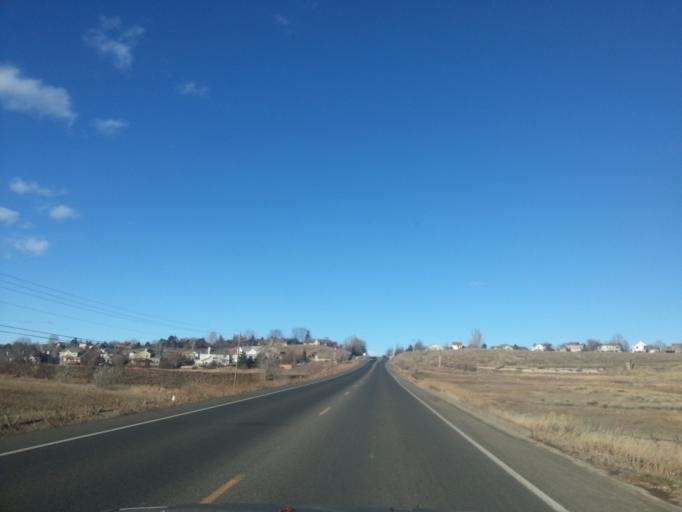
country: US
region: Colorado
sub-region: Larimer County
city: Fort Collins
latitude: 40.5211
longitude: -105.1151
